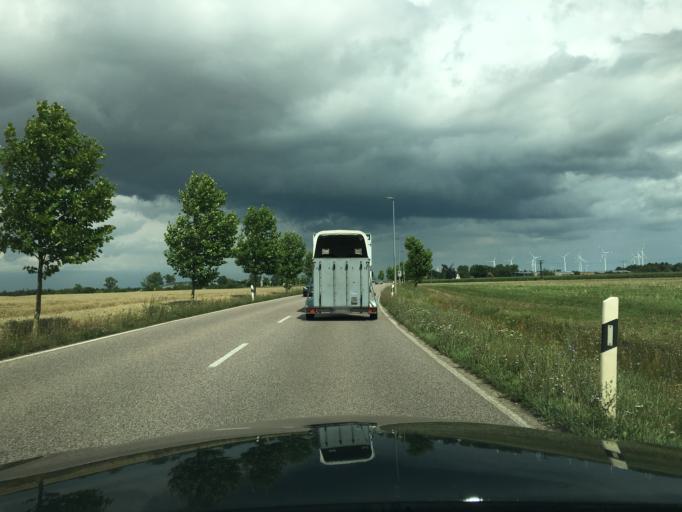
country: DE
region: Saxony-Anhalt
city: Brehna
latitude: 51.5573
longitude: 12.1966
